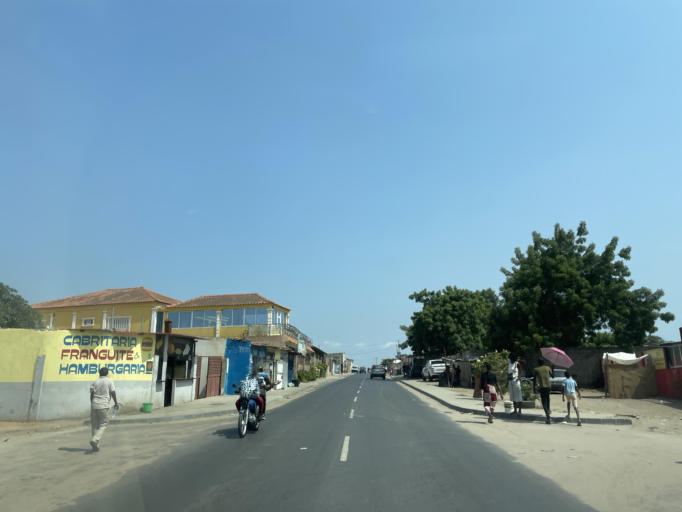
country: AO
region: Luanda
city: Luanda
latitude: -8.9308
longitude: 13.2038
